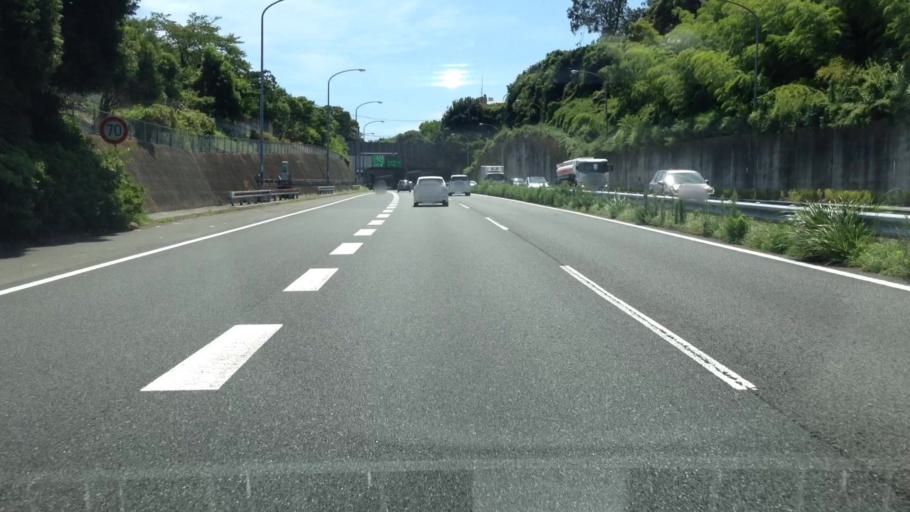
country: JP
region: Kanagawa
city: Yokohama
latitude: 35.4361
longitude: 139.5818
